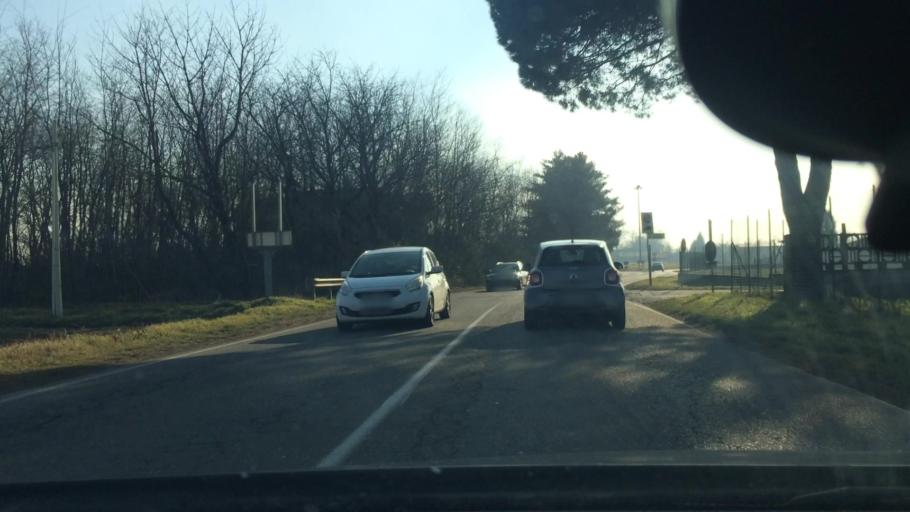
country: IT
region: Lombardy
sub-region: Citta metropolitana di Milano
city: Arluno
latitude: 45.5071
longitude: 8.9300
